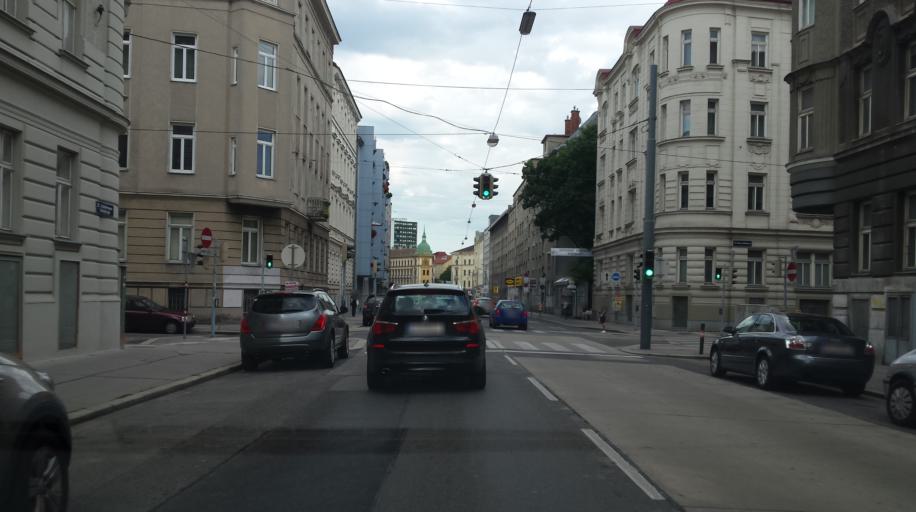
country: AT
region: Vienna
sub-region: Wien Stadt
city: Vienna
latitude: 48.1840
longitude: 16.3232
